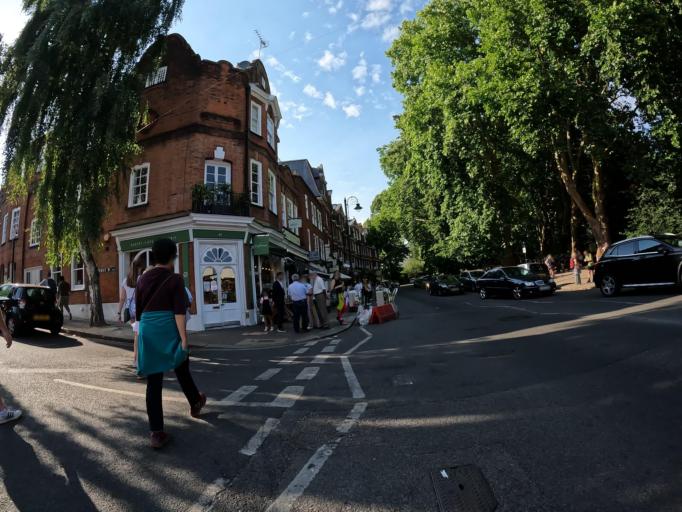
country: GB
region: England
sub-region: Greater London
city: Barnet
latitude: 51.6398
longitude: -0.1965
